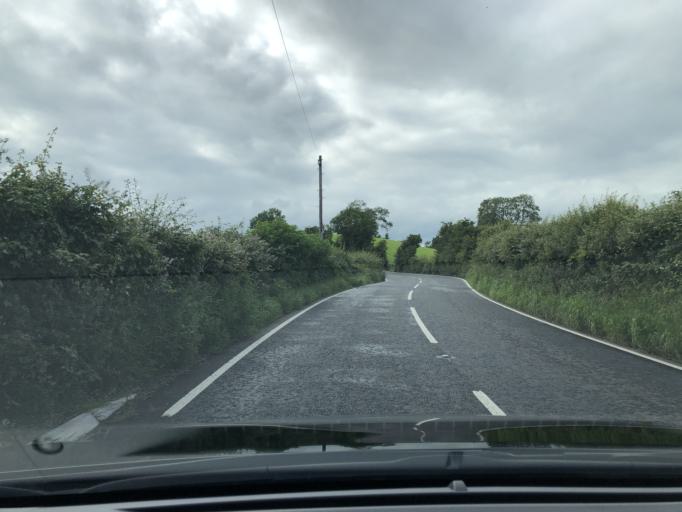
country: GB
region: Northern Ireland
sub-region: Down District
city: Dundrum
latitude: 54.2866
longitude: -5.8280
